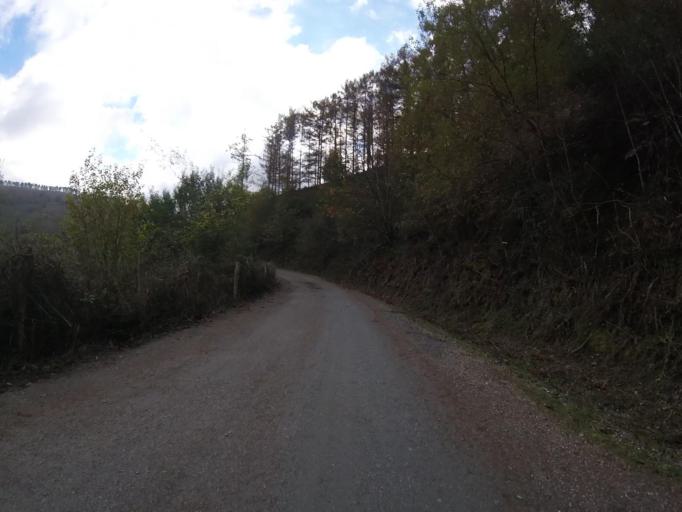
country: ES
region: Navarre
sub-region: Provincia de Navarra
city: Goizueta
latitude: 43.2192
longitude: -1.8373
